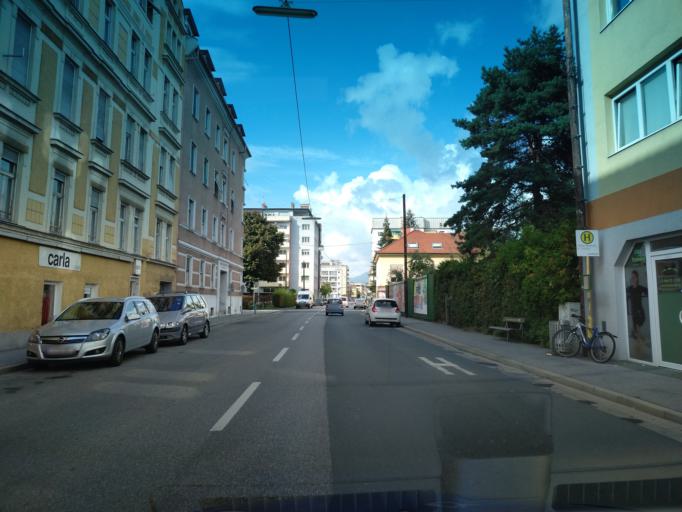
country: AT
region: Styria
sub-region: Graz Stadt
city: Wetzelsdorf
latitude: 47.0650
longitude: 15.4007
